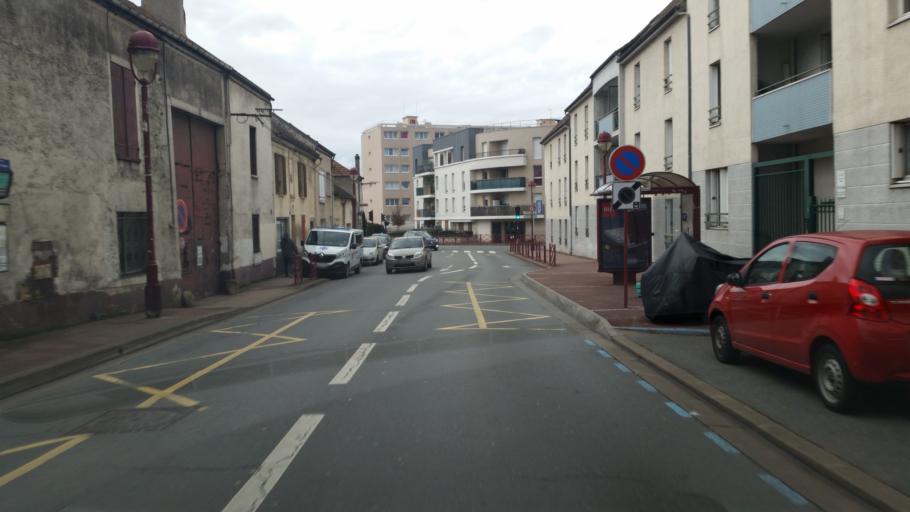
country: FR
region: Ile-de-France
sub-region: Departement du Val-de-Marne
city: Fresnes
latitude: 48.7539
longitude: 2.3256
